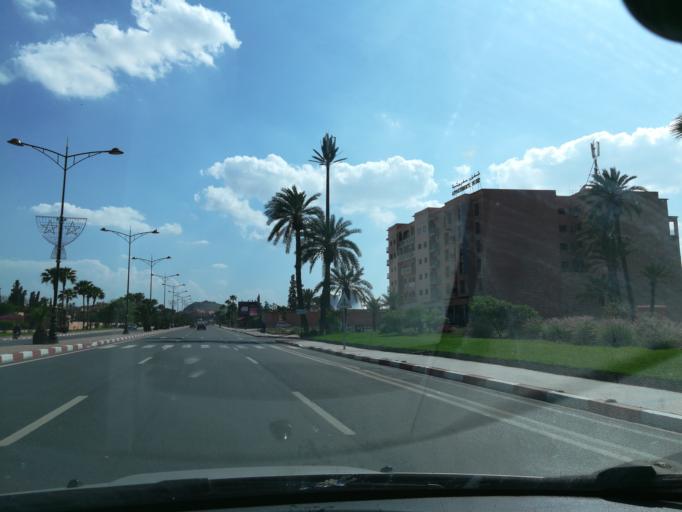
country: MA
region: Marrakech-Tensift-Al Haouz
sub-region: Marrakech
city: Marrakesh
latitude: 31.6618
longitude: -8.0149
